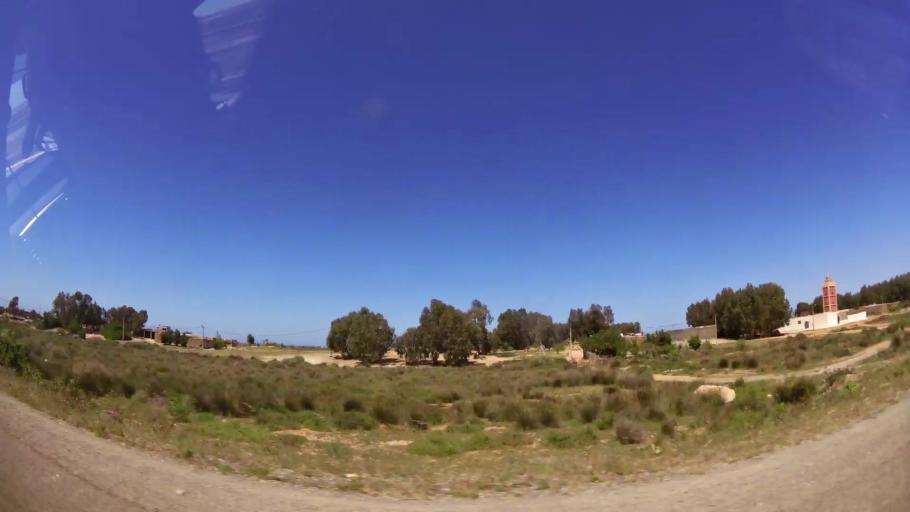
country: MA
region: Oriental
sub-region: Berkane-Taourirt
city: Madagh
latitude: 35.1004
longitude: -2.3338
